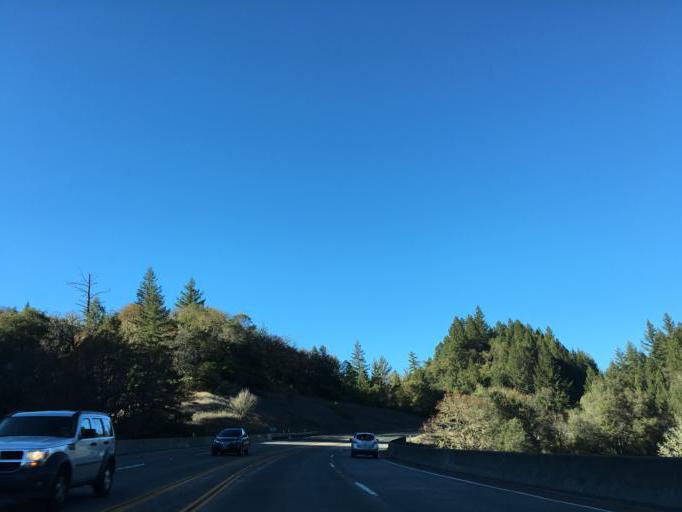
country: US
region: California
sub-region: Mendocino County
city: Brooktrails
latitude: 39.5364
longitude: -123.4162
